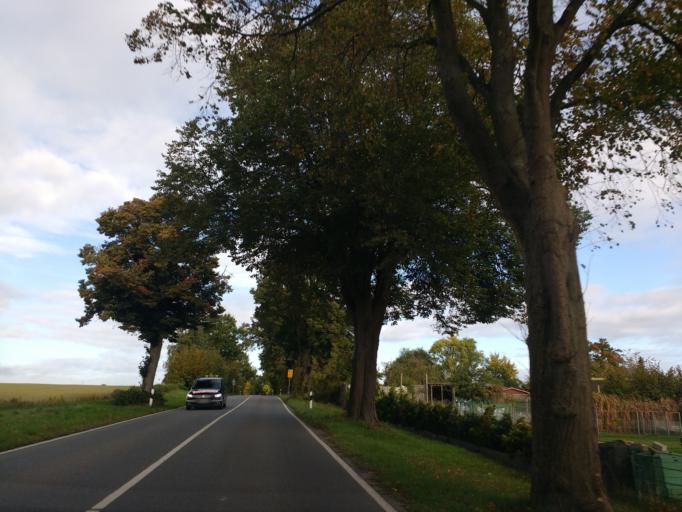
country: DE
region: Schleswig-Holstein
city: Altenkrempe
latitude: 54.1406
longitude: 10.8231
